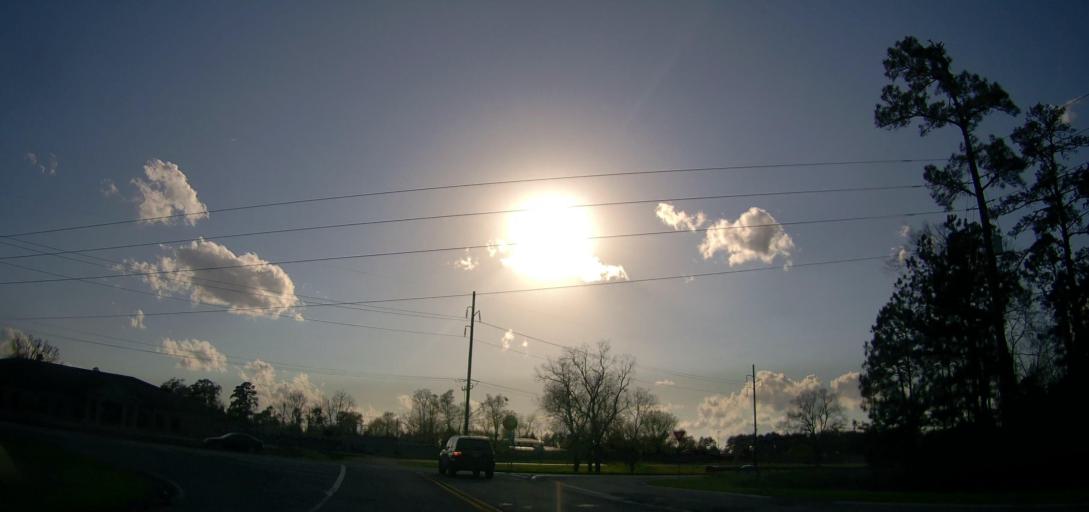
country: US
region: Georgia
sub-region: Baldwin County
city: Milledgeville
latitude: 33.0905
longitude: -83.2493
